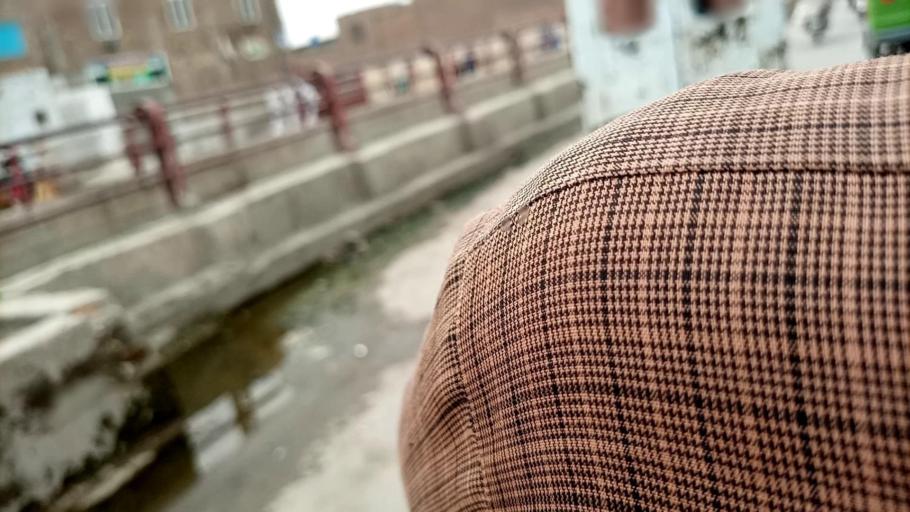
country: PK
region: Khyber Pakhtunkhwa
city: Peshawar
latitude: 34.0183
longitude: 71.5928
